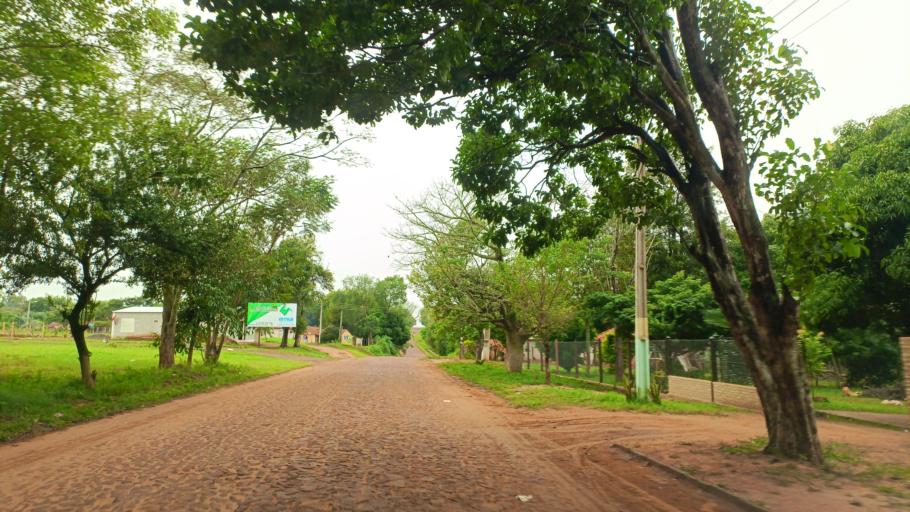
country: PY
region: Misiones
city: Santa Maria
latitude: -26.8610
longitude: -57.0318
